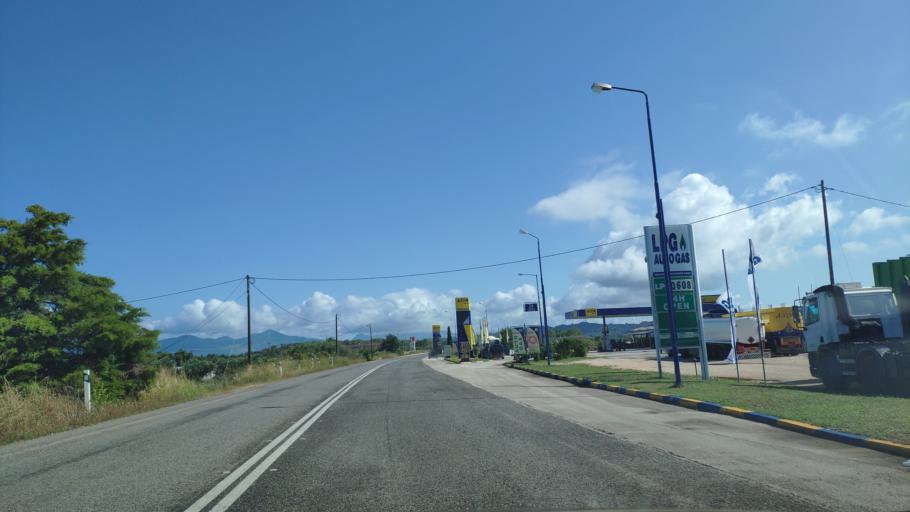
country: GR
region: Epirus
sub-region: Nomos Prevezis
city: Preveza
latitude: 38.9915
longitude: 20.7137
